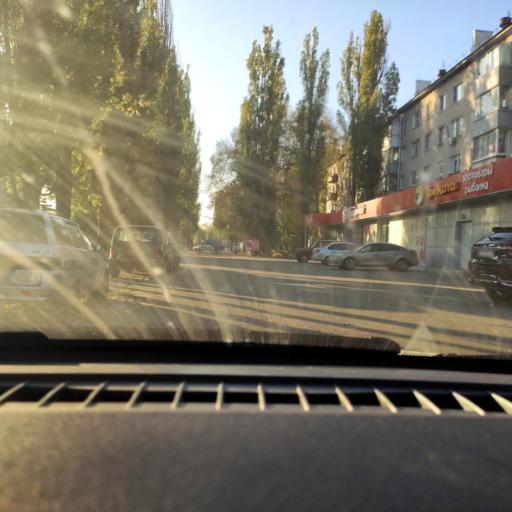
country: RU
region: Voronezj
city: Maslovka
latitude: 51.6333
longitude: 39.2671
